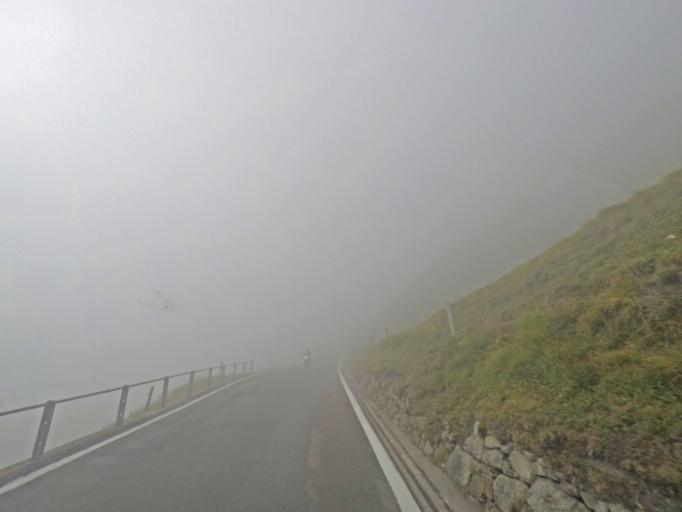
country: CH
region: Uri
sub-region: Uri
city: Andermatt
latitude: 46.5912
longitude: 8.4720
